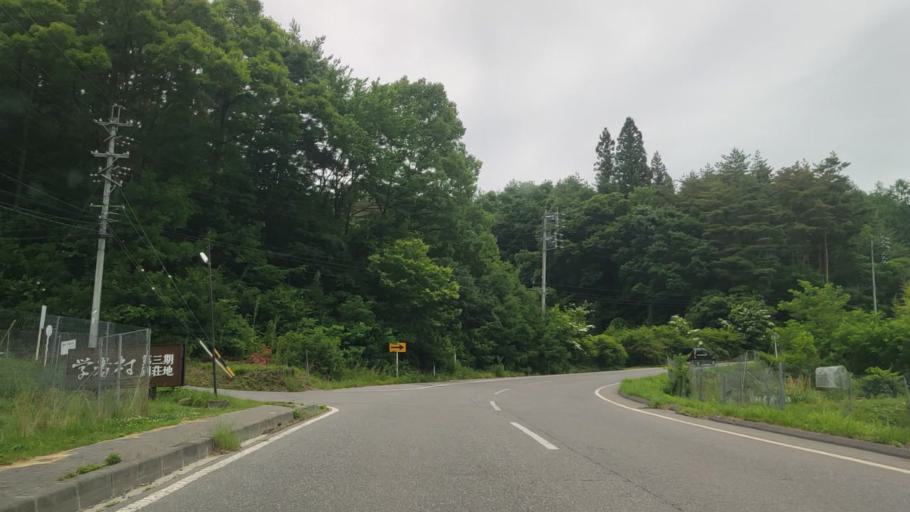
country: JP
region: Nagano
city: Kamimaruko
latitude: 36.2779
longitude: 138.2813
